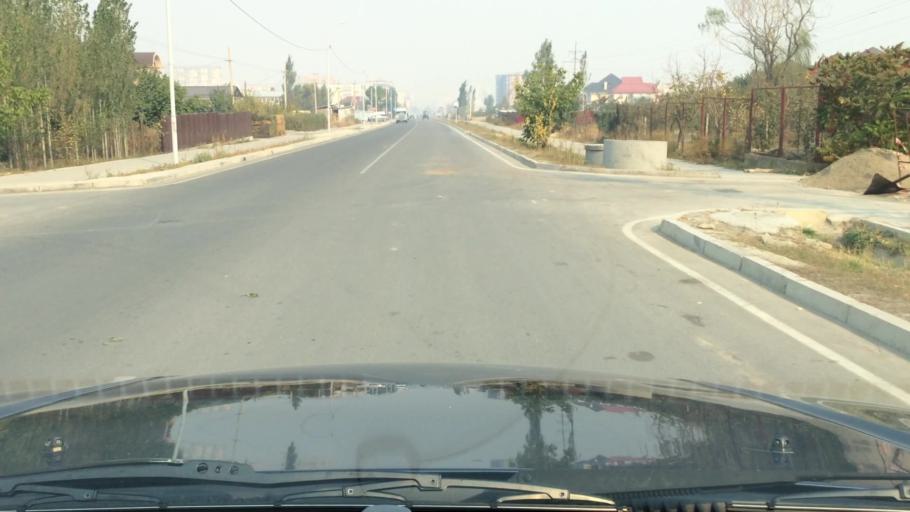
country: KG
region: Chuy
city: Bishkek
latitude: 42.8232
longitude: 74.5699
